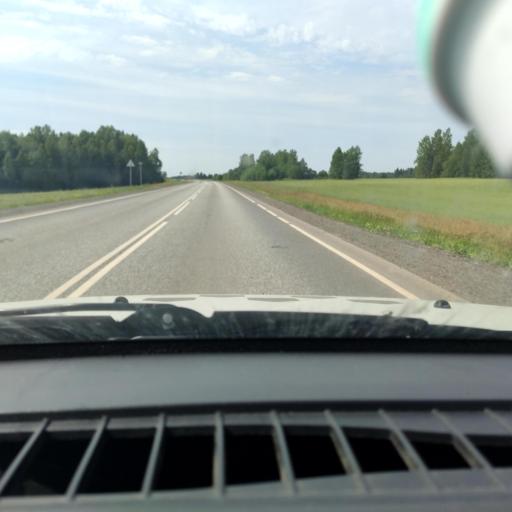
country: RU
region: Perm
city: Siva
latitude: 58.4877
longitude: 54.1302
